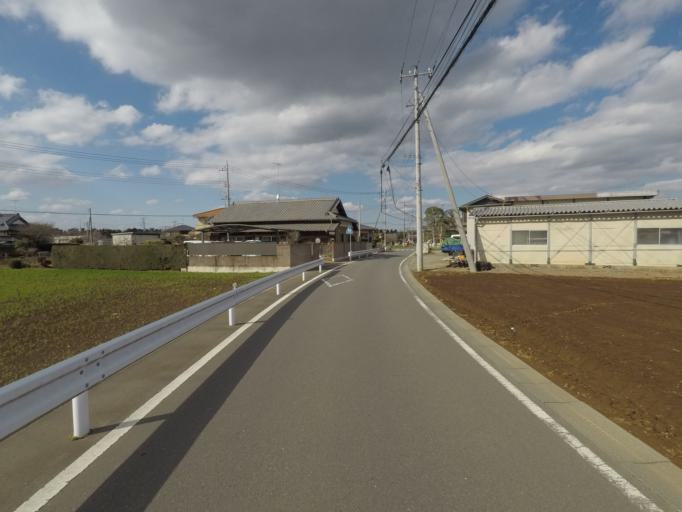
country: JP
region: Ibaraki
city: Naka
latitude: 36.0385
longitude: 140.1423
